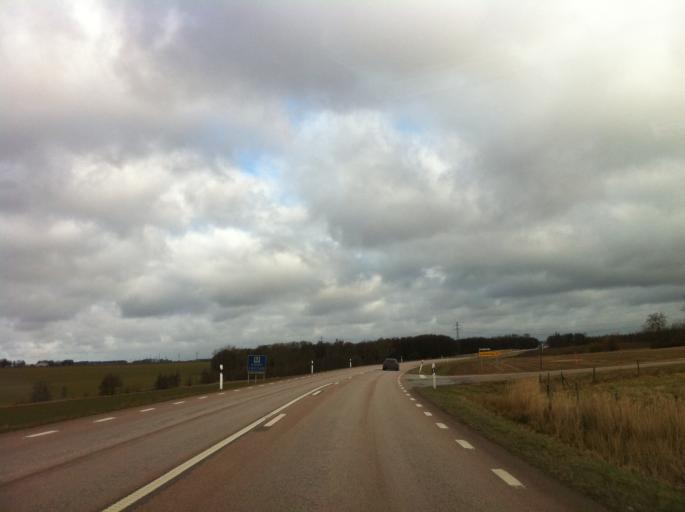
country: SE
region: Skane
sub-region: Landskrona
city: Asmundtorp
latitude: 55.9766
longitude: 12.9374
